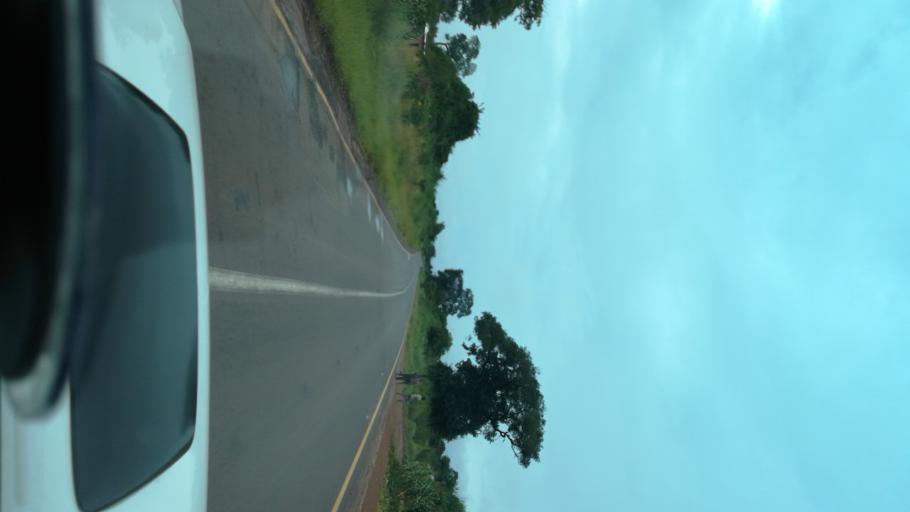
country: CD
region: Katanga
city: Lubumbashi
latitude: -11.3388
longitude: 27.8183
